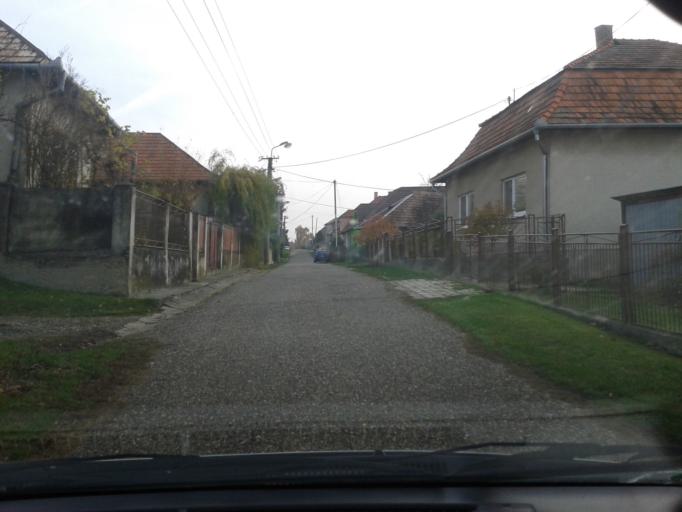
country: SK
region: Nitriansky
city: Svodin
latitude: 48.0386
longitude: 18.4691
